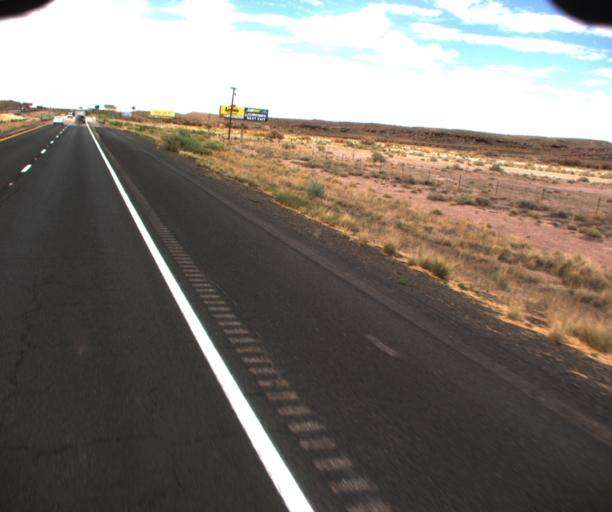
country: US
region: Arizona
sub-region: Navajo County
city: Joseph City
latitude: 34.9452
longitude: -110.2925
